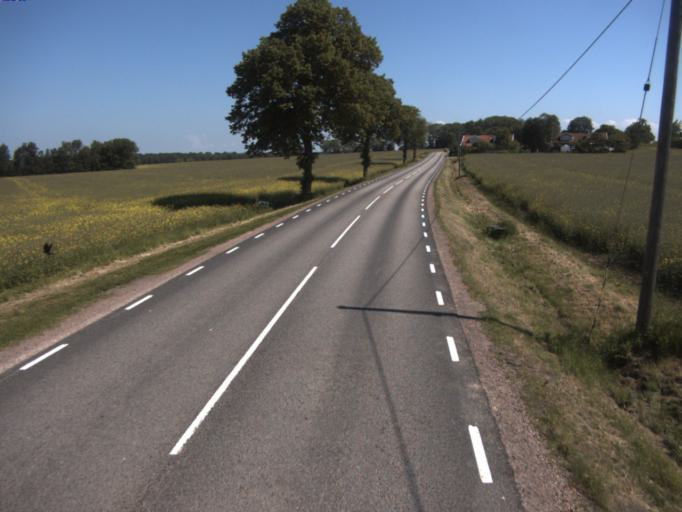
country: SE
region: Skane
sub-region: Helsingborg
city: Barslov
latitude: 56.0387
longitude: 12.7932
